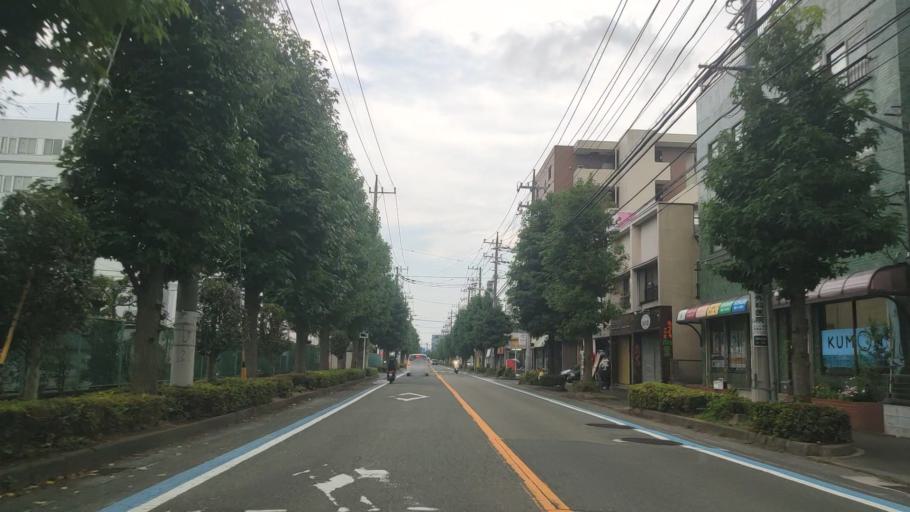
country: JP
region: Kanagawa
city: Minami-rinkan
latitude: 35.5056
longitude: 139.4489
